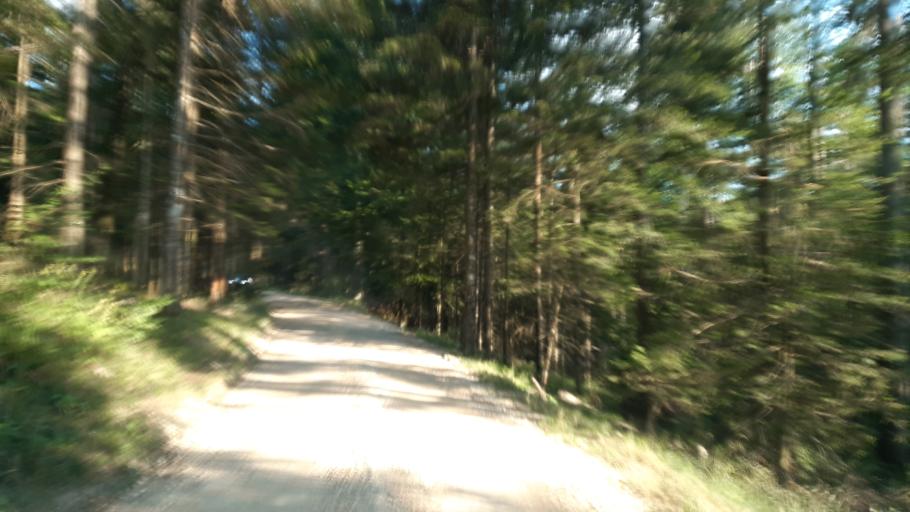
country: SI
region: Dolenjske Toplice
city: Dolenjske Toplice
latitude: 45.7034
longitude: 15.0089
